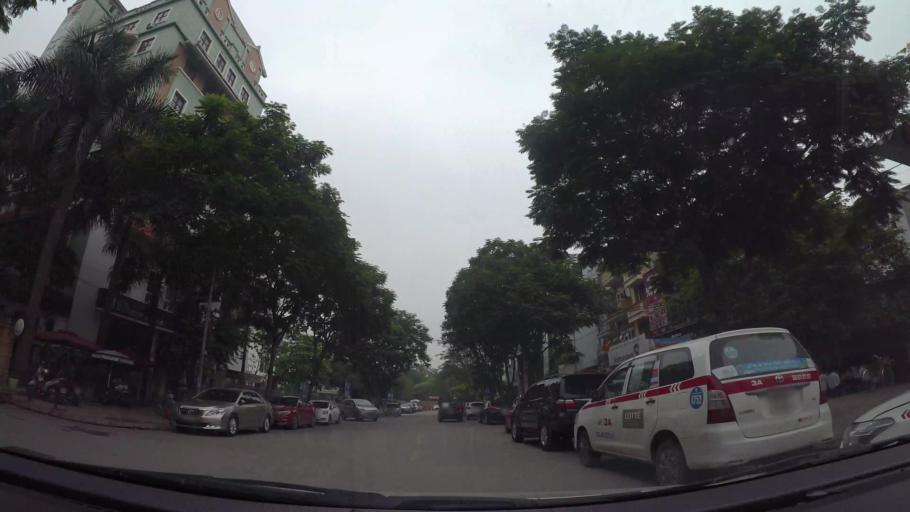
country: VN
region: Ha Noi
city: Cau Giay
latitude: 21.0333
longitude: 105.8187
